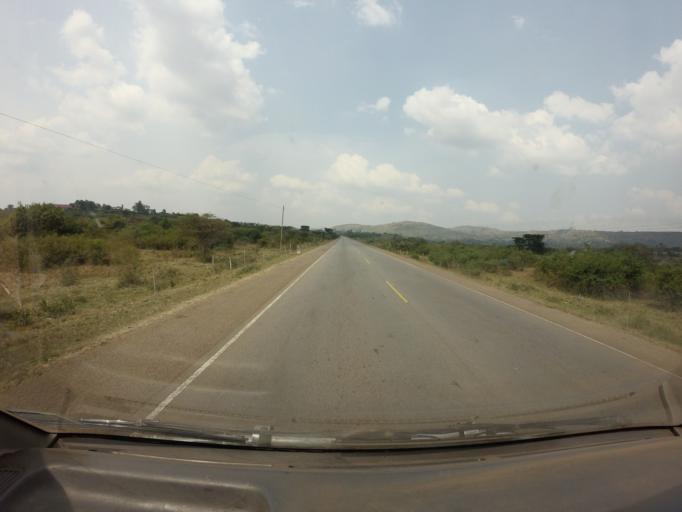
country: UG
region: Central Region
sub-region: Lyantonde District
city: Lyantonde
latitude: -0.3846
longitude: 31.2173
